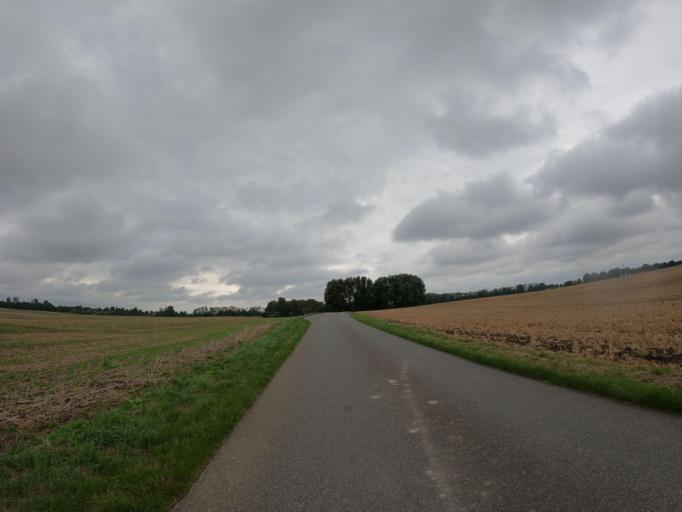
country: DE
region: Mecklenburg-Vorpommern
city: Poseritz
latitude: 54.2925
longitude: 13.3158
